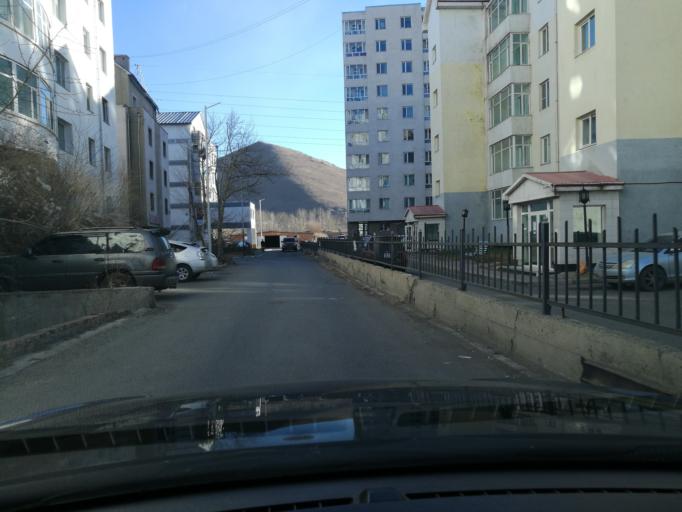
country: MN
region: Ulaanbaatar
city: Ulaanbaatar
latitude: 47.8907
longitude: 106.9002
